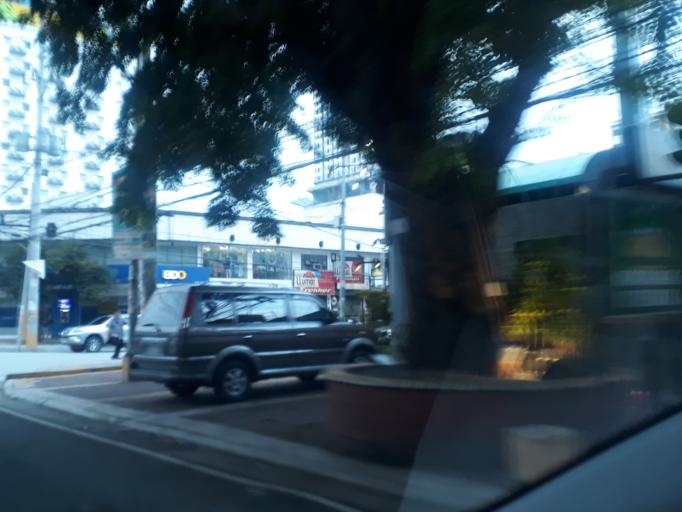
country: PH
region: Metro Manila
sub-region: Quezon City
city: Quezon City
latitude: 14.6344
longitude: 121.0378
